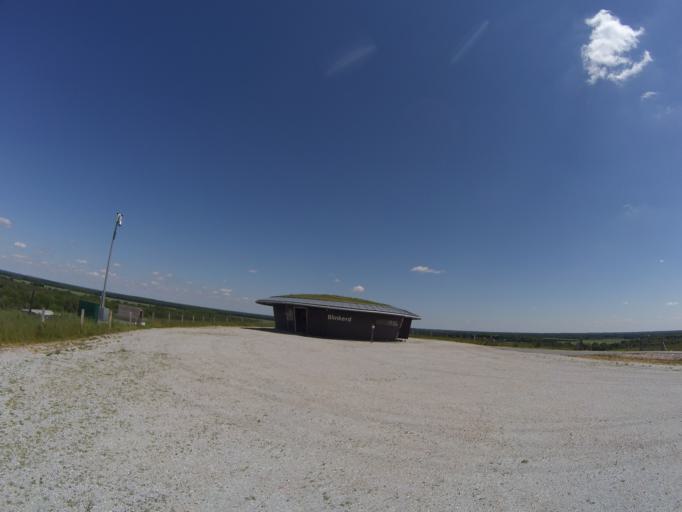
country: NL
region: Drenthe
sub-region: Gemeente Hoogeveen
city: Hoogeveen
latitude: 52.7912
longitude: 6.5240
